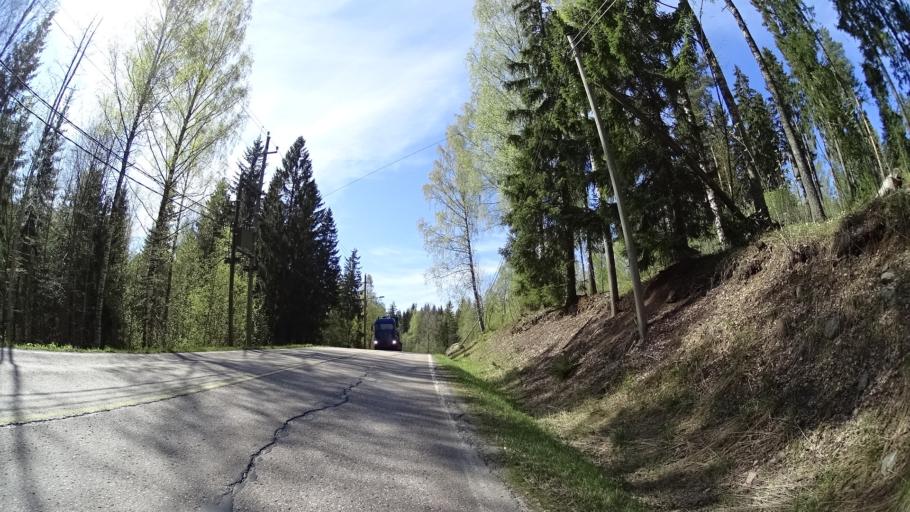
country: FI
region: Uusimaa
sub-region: Helsinki
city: Nurmijaervi
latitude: 60.3885
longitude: 24.8368
